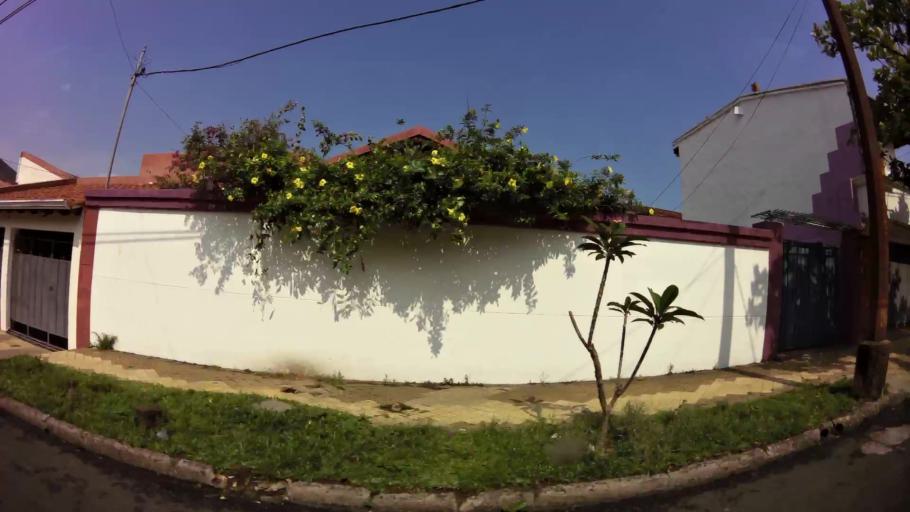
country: PY
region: Presidente Hayes
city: Nanawa
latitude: -25.2911
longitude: -57.6617
